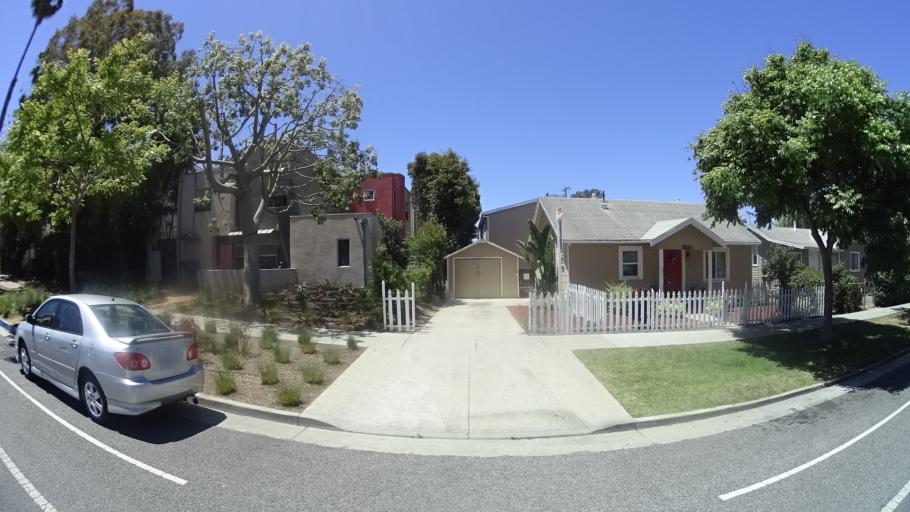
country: US
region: California
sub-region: Los Angeles County
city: Santa Monica
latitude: 34.0203
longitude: -118.4758
